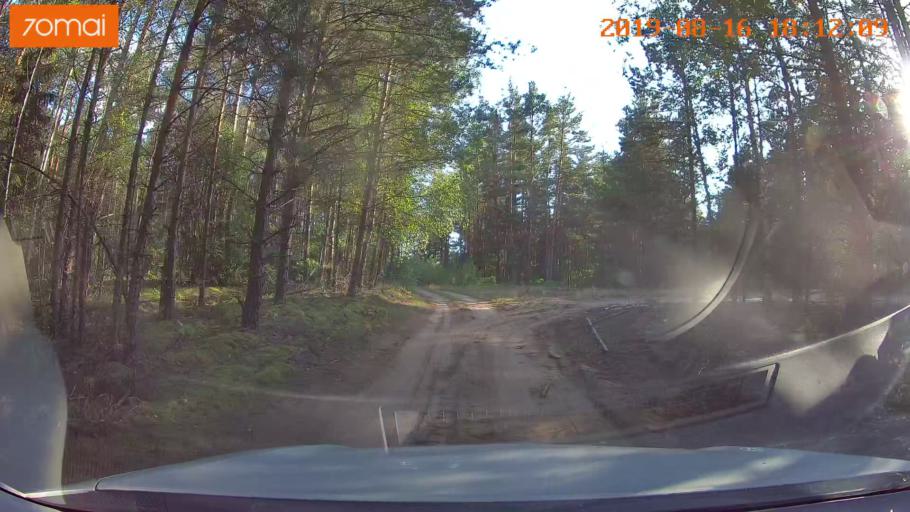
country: BY
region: Mogilev
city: Asipovichy
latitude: 53.2136
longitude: 28.6455
